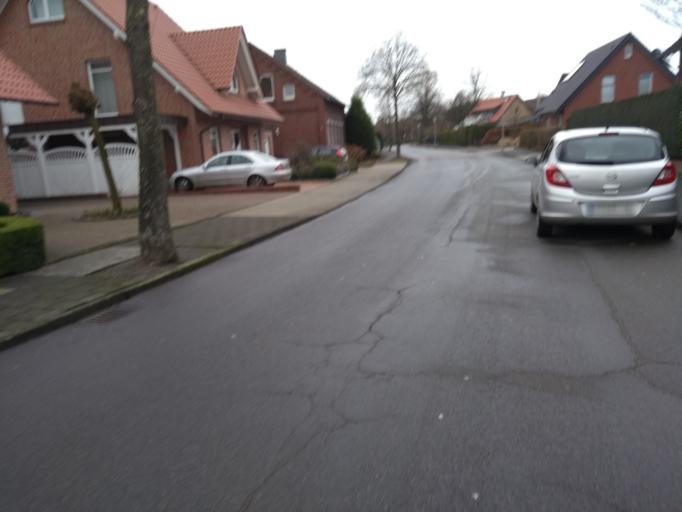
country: DE
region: North Rhine-Westphalia
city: Ibbenburen
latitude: 52.2817
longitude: 7.7030
